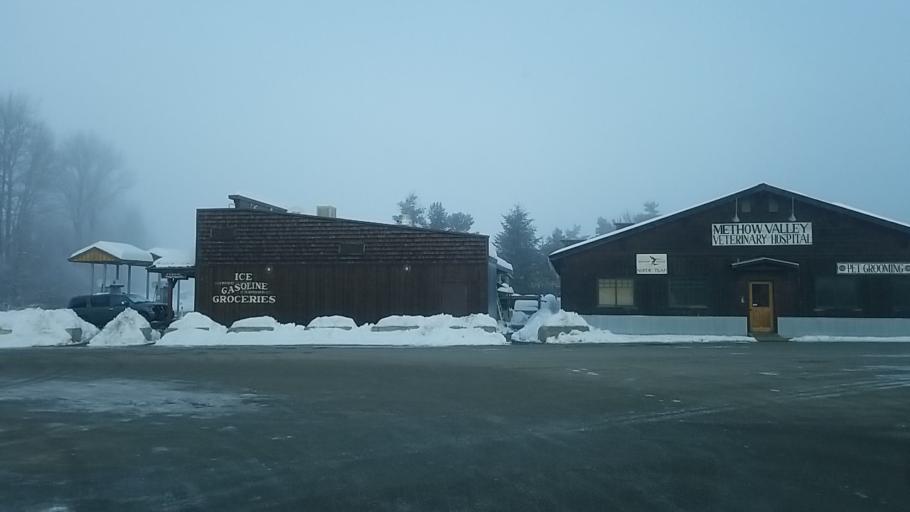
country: US
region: Washington
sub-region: Okanogan County
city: Brewster
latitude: 48.4670
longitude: -120.1749
